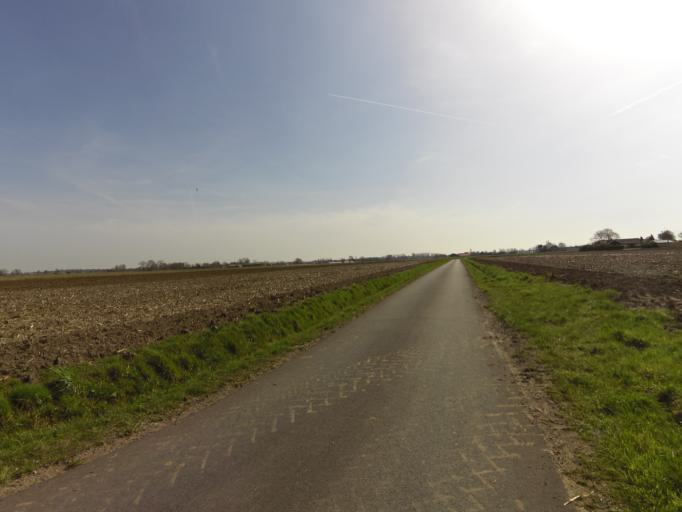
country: BE
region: Flanders
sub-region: Provincie West-Vlaanderen
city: Koekelare
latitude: 51.1104
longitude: 2.9461
